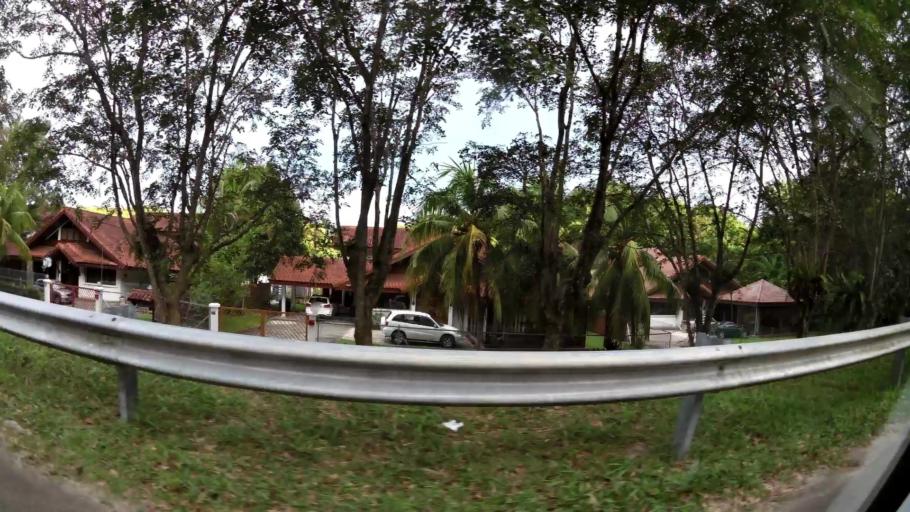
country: BN
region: Brunei and Muara
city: Bandar Seri Begawan
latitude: 4.9058
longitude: 114.9945
